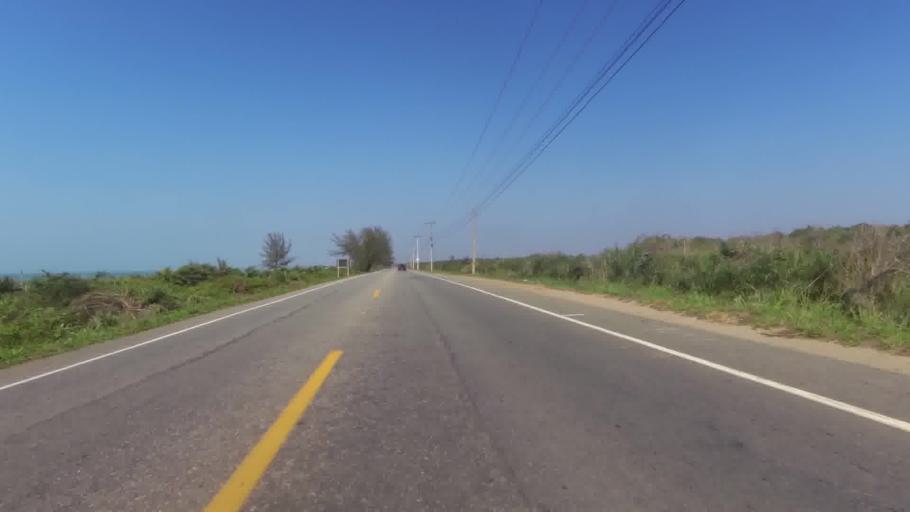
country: BR
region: Espirito Santo
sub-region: Itapemirim
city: Itapemirim
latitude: -20.9328
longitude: -40.8003
